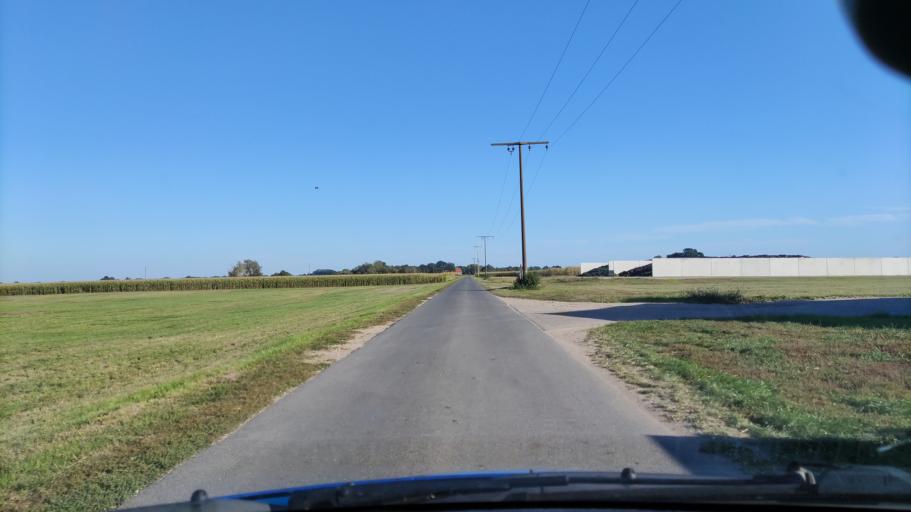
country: DE
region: Lower Saxony
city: Hitzacker
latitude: 53.1326
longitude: 11.0715
